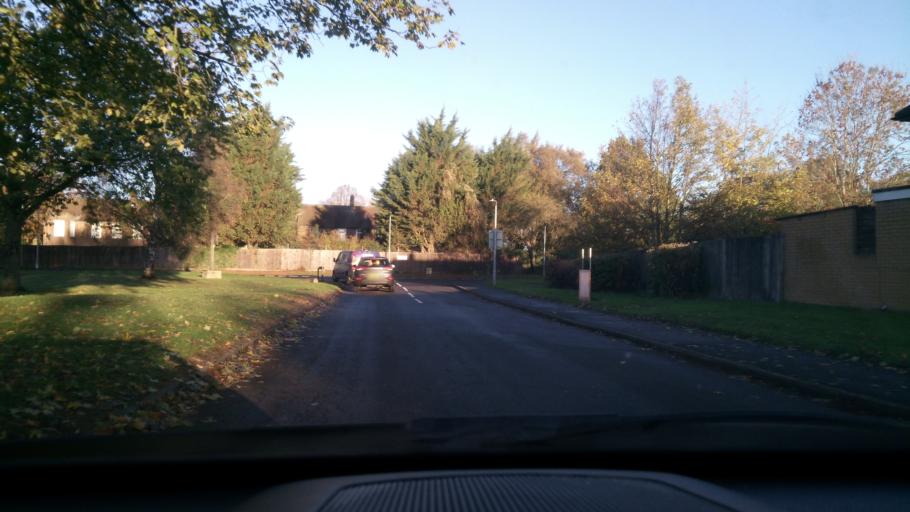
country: GB
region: England
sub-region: Peterborough
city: Wittering
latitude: 52.6109
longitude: -0.4419
